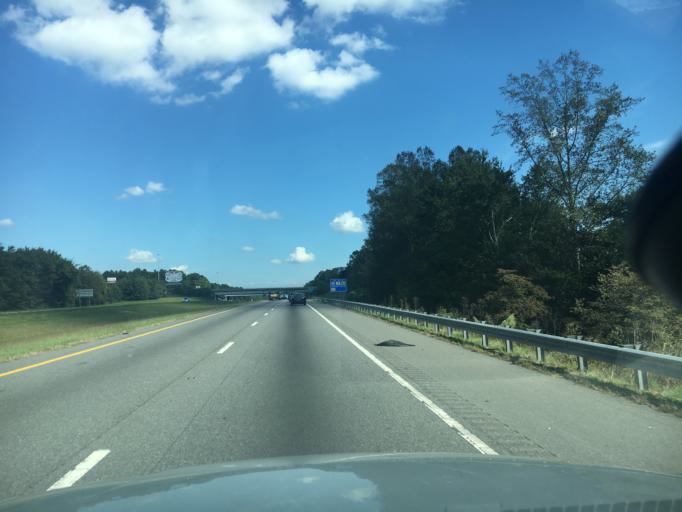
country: US
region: North Carolina
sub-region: Catawba County
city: Conover
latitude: 35.7119
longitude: -81.2335
